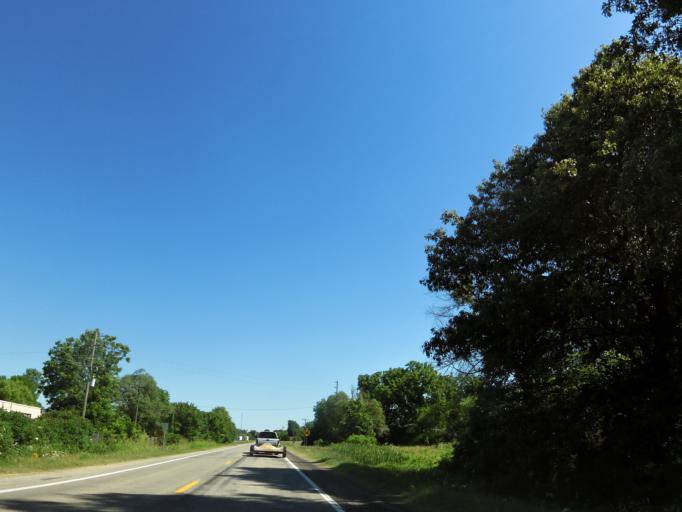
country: US
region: Arkansas
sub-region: Clay County
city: Piggott
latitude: 36.4434
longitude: -90.1472
